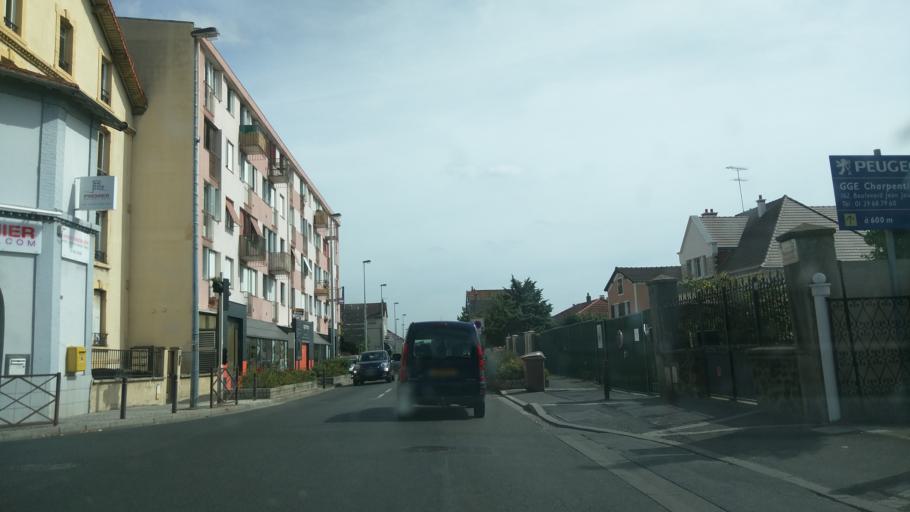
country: FR
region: Ile-de-France
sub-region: Departement des Yvelines
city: Houilles
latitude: 48.9199
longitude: 2.1923
